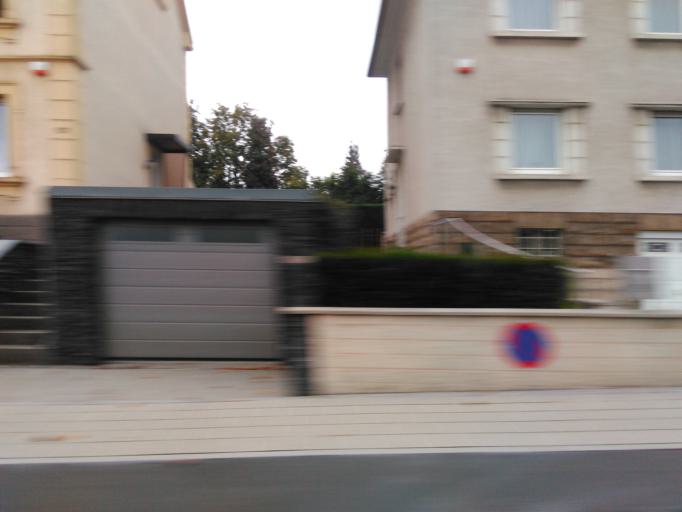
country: LU
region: Luxembourg
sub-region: Canton d'Esch-sur-Alzette
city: Esch-sur-Alzette
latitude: 49.5039
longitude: 5.9671
